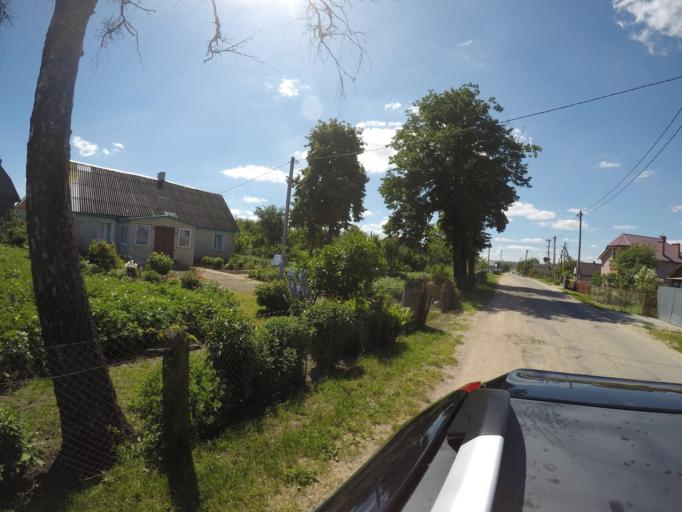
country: BY
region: Grodnenskaya
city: Hrodna
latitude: 53.7252
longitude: 23.8492
